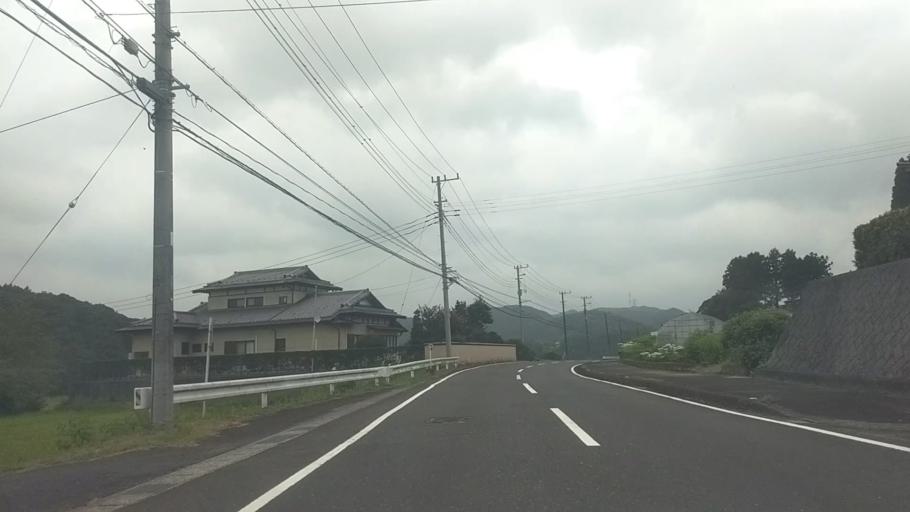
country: JP
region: Chiba
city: Kawaguchi
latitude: 35.2596
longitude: 140.0522
